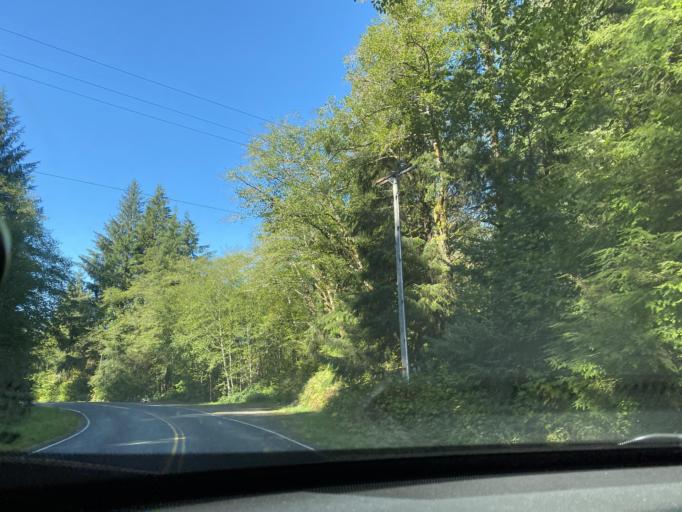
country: US
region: Washington
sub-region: Clallam County
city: Forks
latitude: 47.9514
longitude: -124.4682
